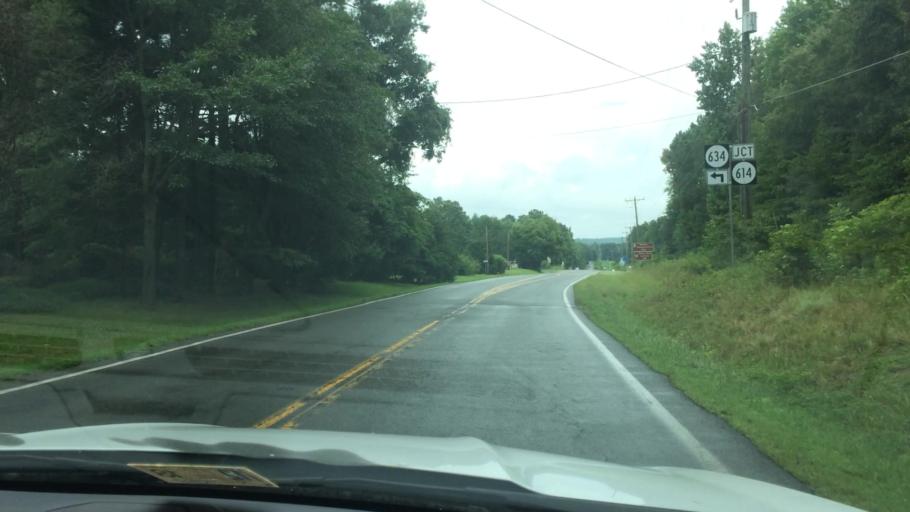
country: US
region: Virginia
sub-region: Charles City County
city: Charles City
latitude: 37.4111
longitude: -77.0455
